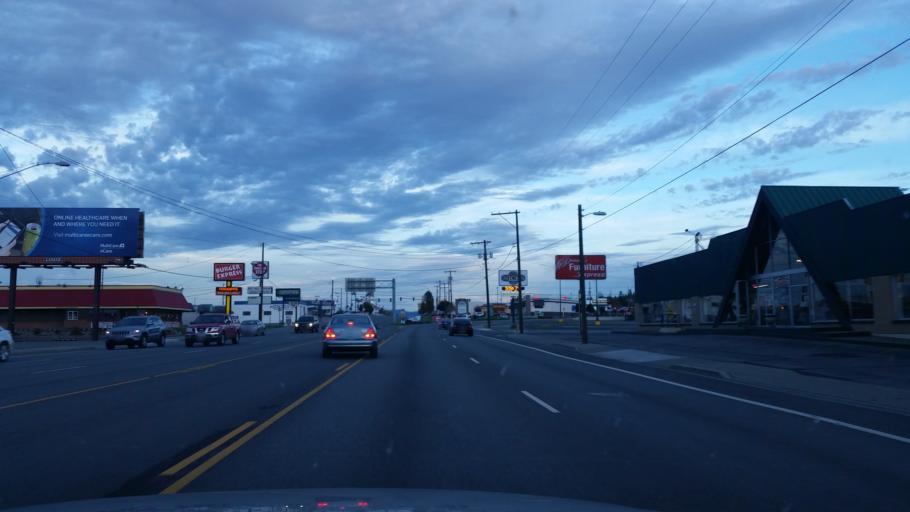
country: US
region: Washington
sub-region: Spokane County
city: Dishman
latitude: 47.6570
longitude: -117.3186
